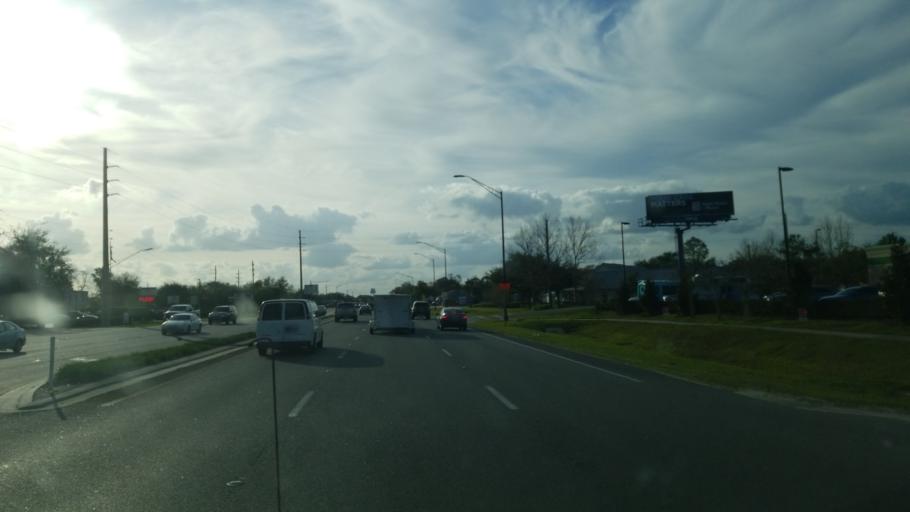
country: US
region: Florida
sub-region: Osceola County
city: Saint Cloud
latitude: 28.2460
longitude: -81.2664
